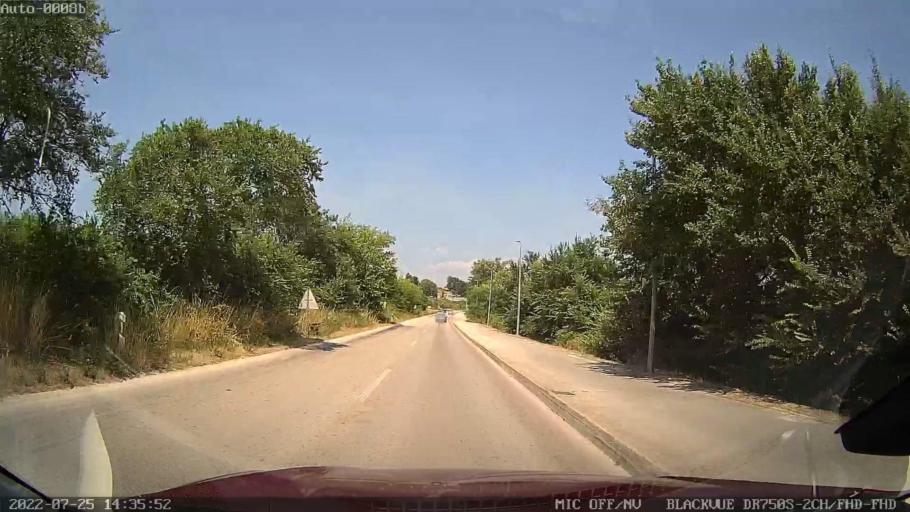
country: HR
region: Zadarska
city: Galovac
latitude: 44.1070
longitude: 15.3808
